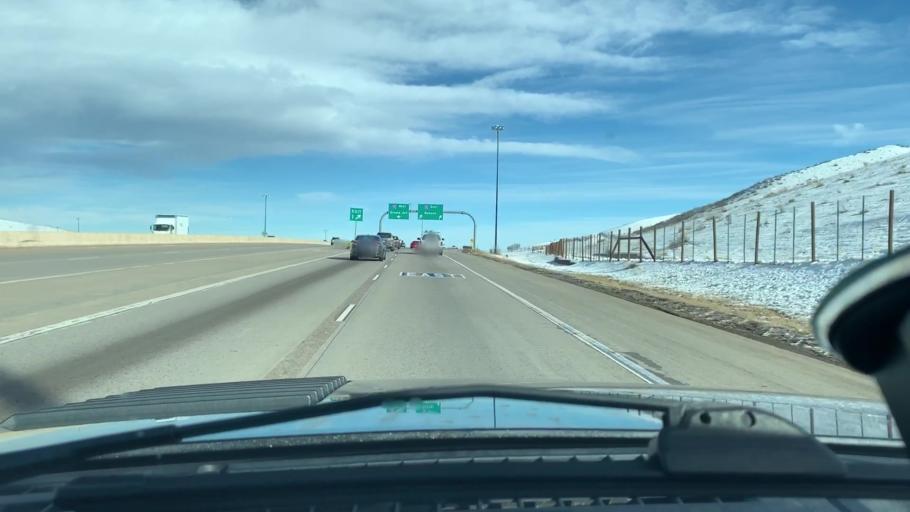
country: US
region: Colorado
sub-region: Jefferson County
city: West Pleasant View
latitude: 39.7065
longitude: -105.1925
